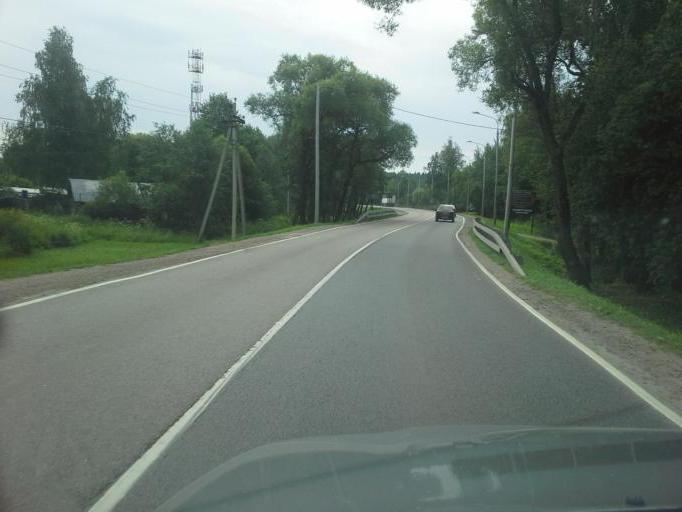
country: RU
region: Moskovskaya
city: Kokoshkino
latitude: 55.5700
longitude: 37.1452
